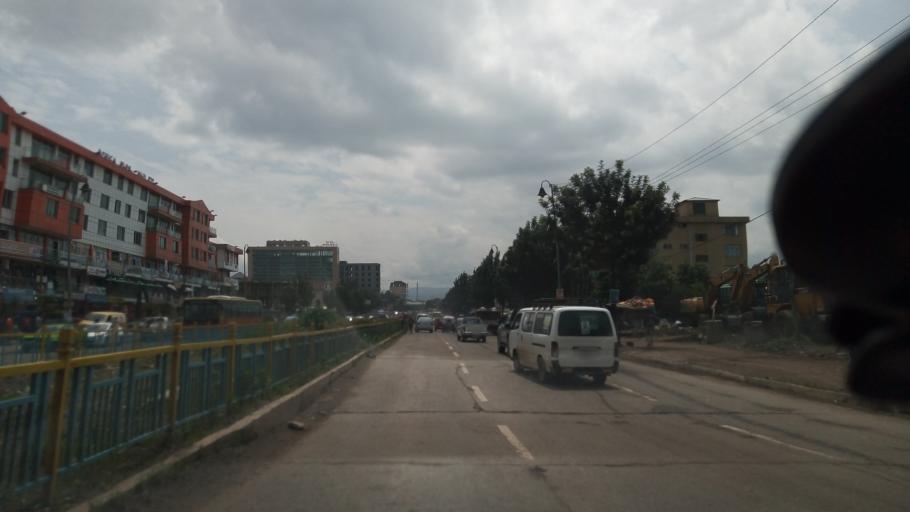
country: ET
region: Adis Abeba
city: Addis Ababa
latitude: 8.9663
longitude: 38.7205
